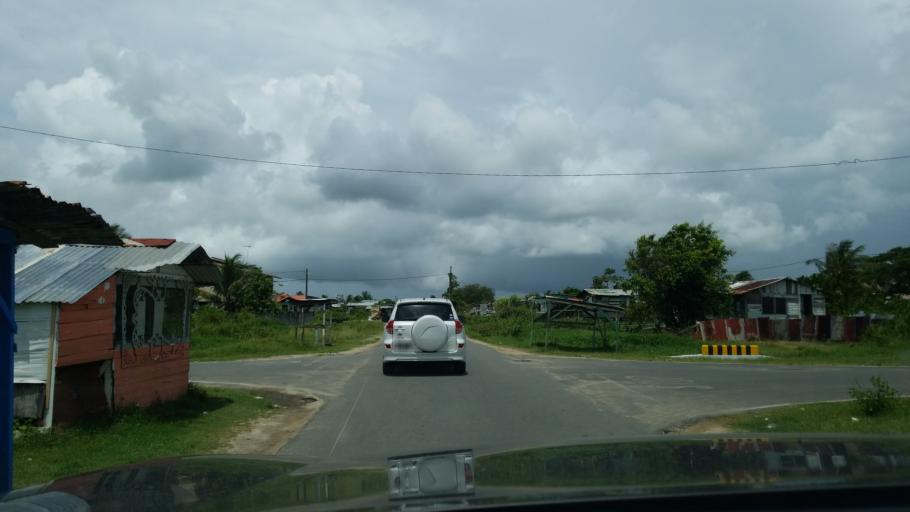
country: GY
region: Demerara-Mahaica
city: Georgetown
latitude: 6.8027
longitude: -58.1229
